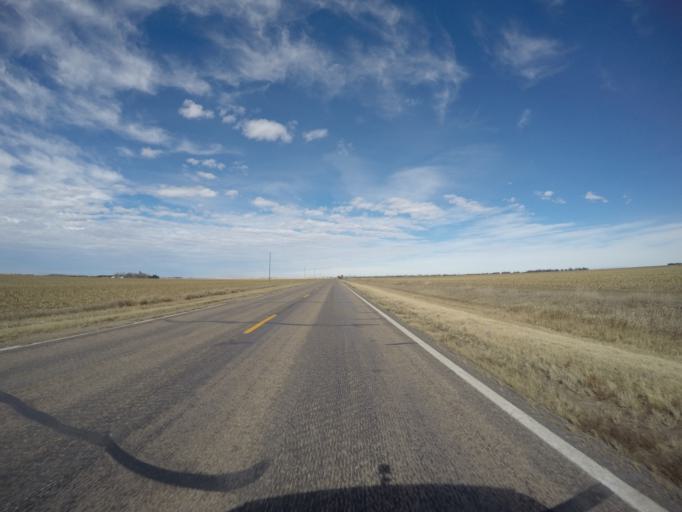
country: US
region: Nebraska
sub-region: Franklin County
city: Franklin
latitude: 40.2424
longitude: -98.9524
